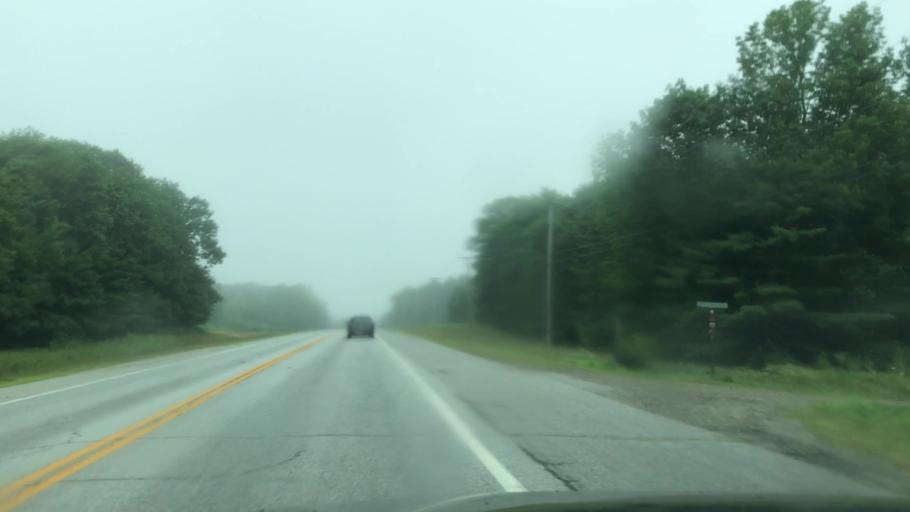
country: US
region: Maine
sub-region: Lincoln County
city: Nobleboro
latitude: 44.0858
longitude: -69.4723
